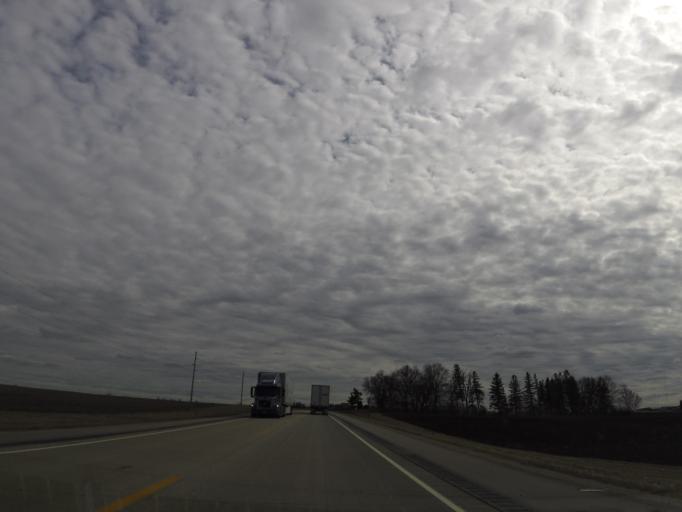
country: US
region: Minnesota
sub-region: Fillmore County
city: Spring Valley
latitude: 43.6076
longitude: -92.3894
